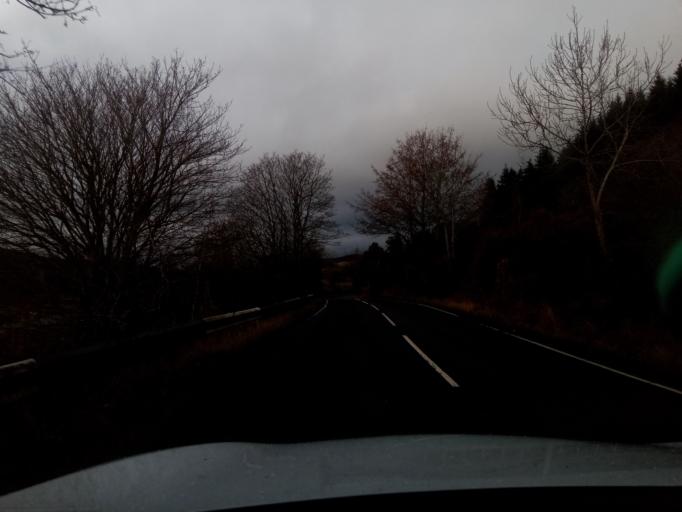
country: GB
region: Scotland
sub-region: The Scottish Borders
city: Innerleithen
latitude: 55.6163
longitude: -3.0766
